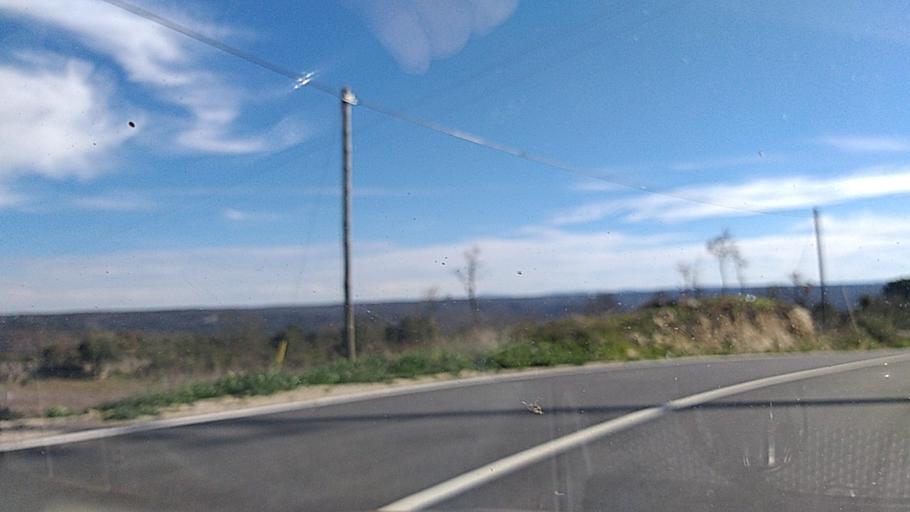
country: ES
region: Castille and Leon
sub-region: Provincia de Salamanca
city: Fuentes de Onoro
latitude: 40.5988
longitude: -6.9379
